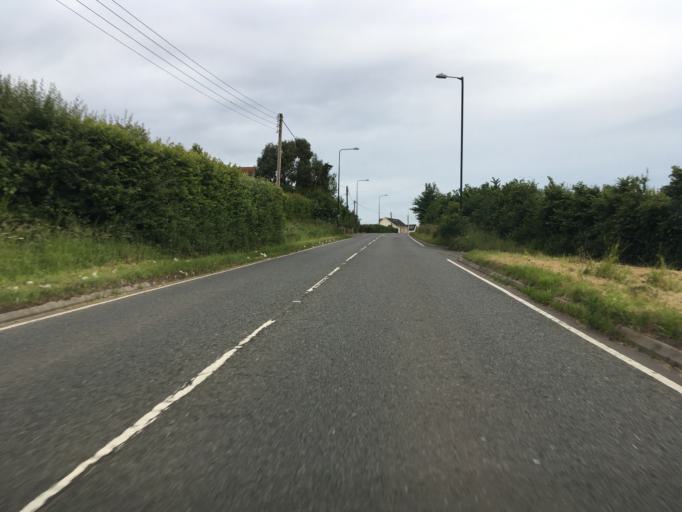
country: GB
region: England
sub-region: North Somerset
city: Easton-in-Gordano
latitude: 51.4717
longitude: -2.6929
